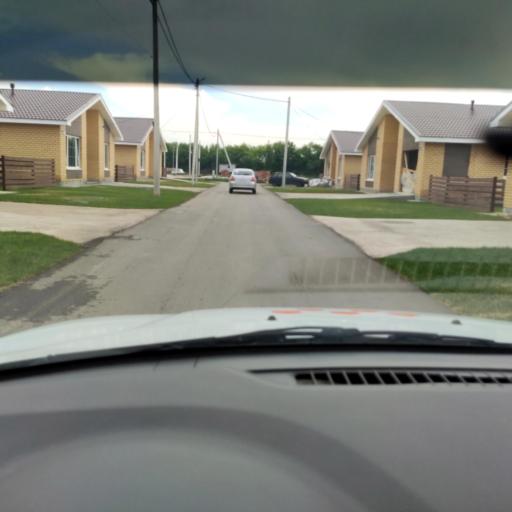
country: RU
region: Samara
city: Podstepki
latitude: 53.5735
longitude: 49.0868
